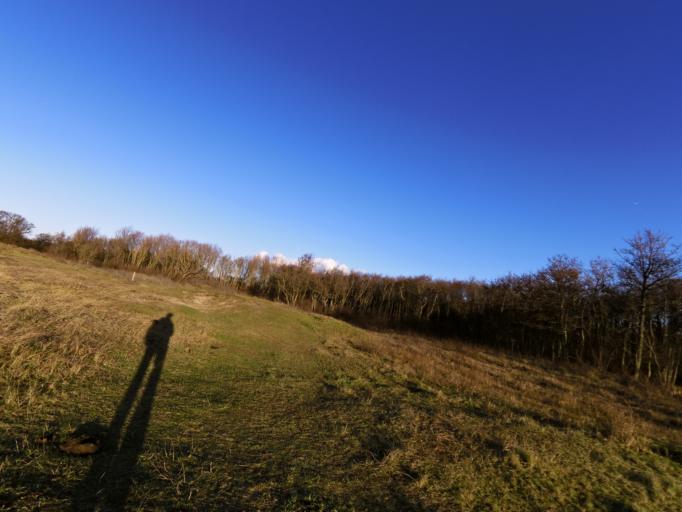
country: NL
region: South Holland
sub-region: Gemeente Goeree-Overflakkee
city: Goedereede
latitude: 51.8931
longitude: 4.0431
